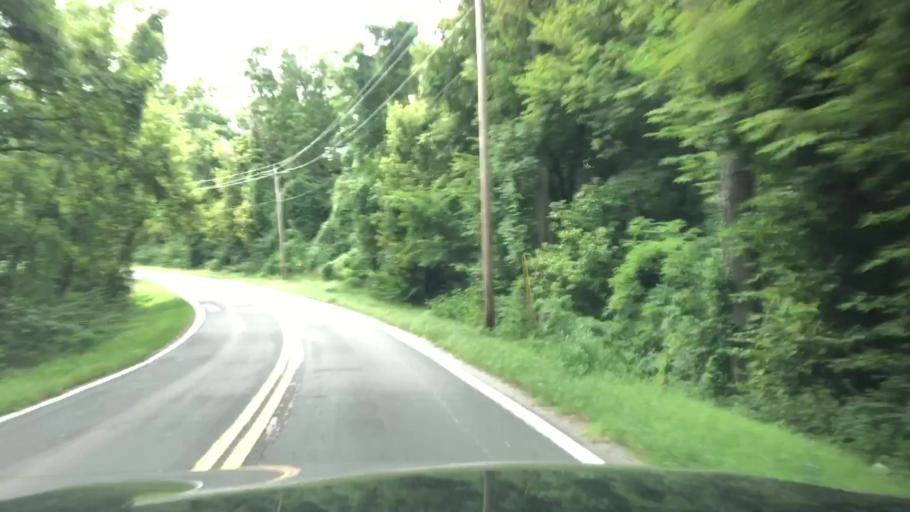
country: US
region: Missouri
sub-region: Saint Louis County
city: Hazelwood
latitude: 38.8154
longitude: -90.3759
